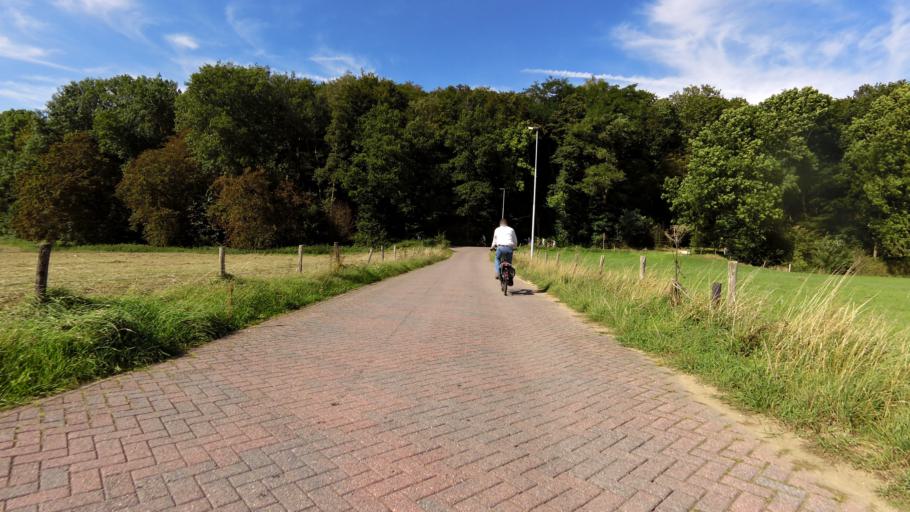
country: NL
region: Gelderland
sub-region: Gemeente Overbetuwe
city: Driel
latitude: 51.9688
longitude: 5.8059
